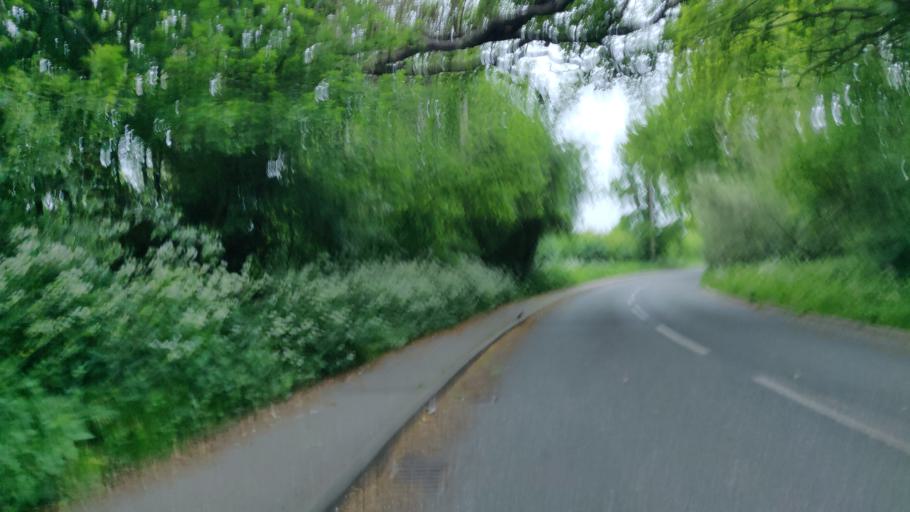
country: GB
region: England
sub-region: West Sussex
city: Partridge Green
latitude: 50.9642
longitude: -0.3029
